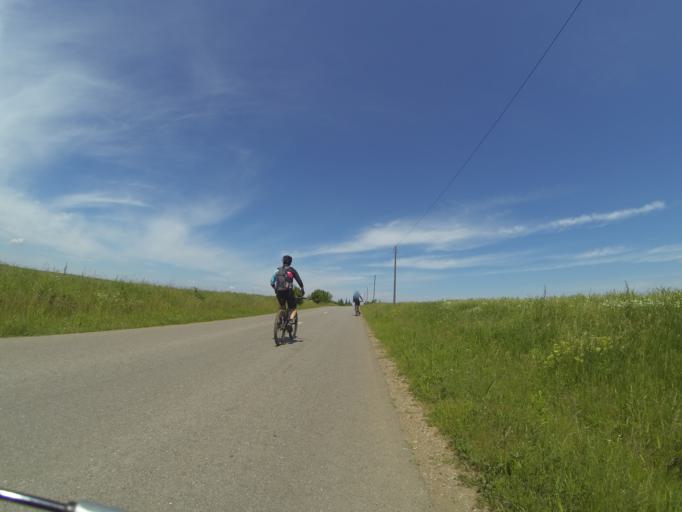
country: RO
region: Dolj
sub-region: Comuna Diosti
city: Radomir
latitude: 44.1492
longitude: 24.1637
